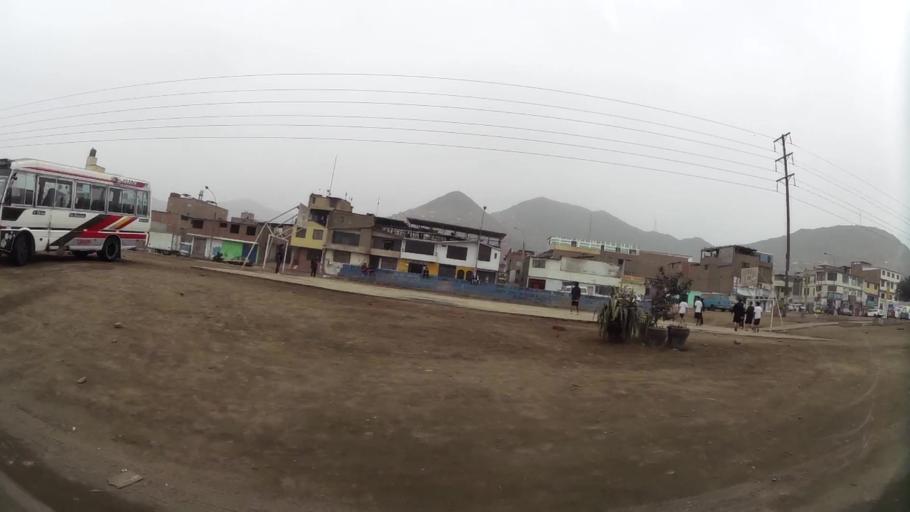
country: PE
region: Lima
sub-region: Lima
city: Surco
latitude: -12.1707
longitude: -76.9468
